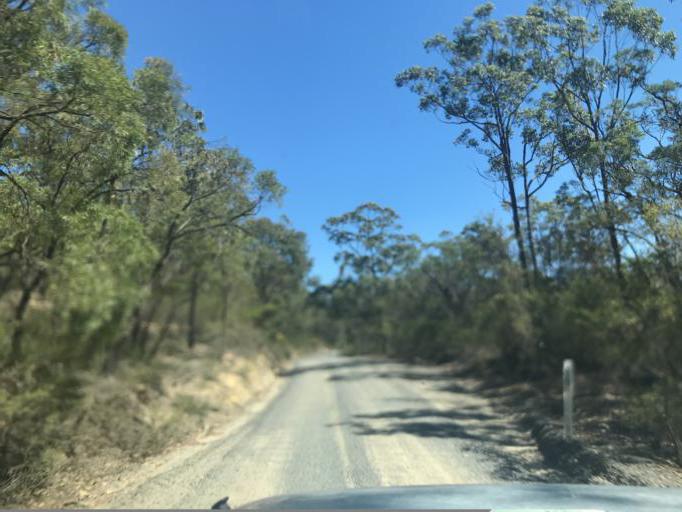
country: AU
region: New South Wales
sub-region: Wyong Shire
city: Little Jilliby
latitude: -33.1483
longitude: 151.0818
